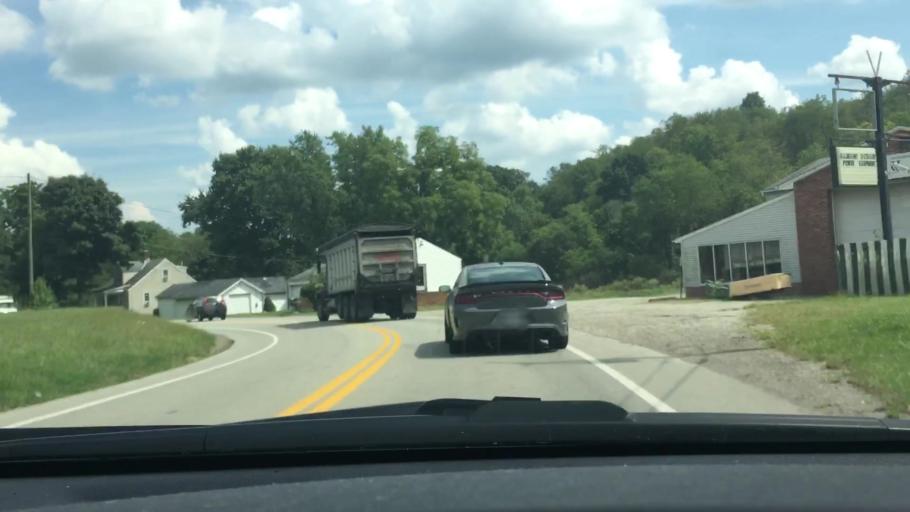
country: US
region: Pennsylvania
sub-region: Washington County
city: McMurray
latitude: 40.2461
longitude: -80.0454
